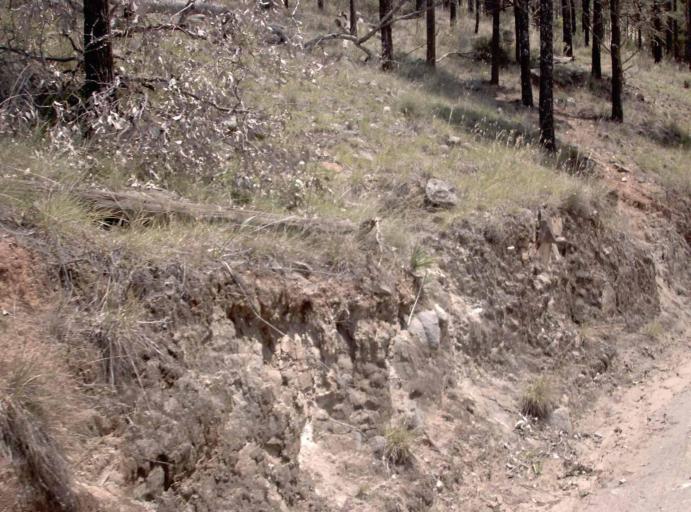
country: AU
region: New South Wales
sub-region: Snowy River
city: Jindabyne
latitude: -36.9072
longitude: 148.4158
